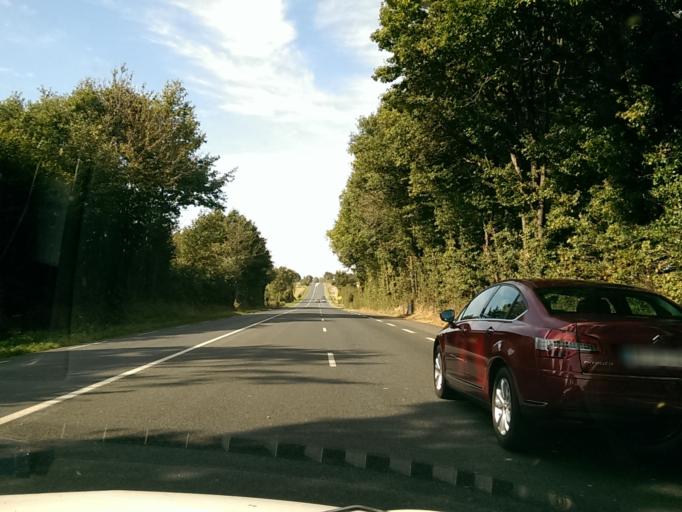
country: FR
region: Pays de la Loire
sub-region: Departement de Maine-et-Loire
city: Vihiers
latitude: 47.1496
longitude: -0.4868
